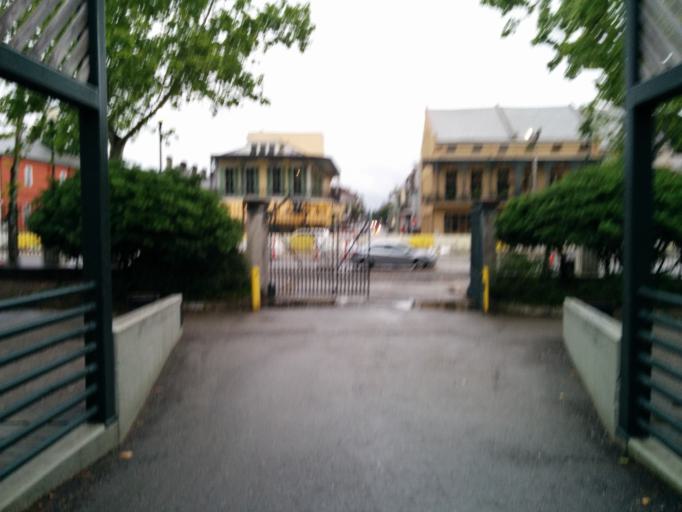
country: US
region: Louisiana
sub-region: Orleans Parish
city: New Orleans
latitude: 29.9624
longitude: -90.0673
